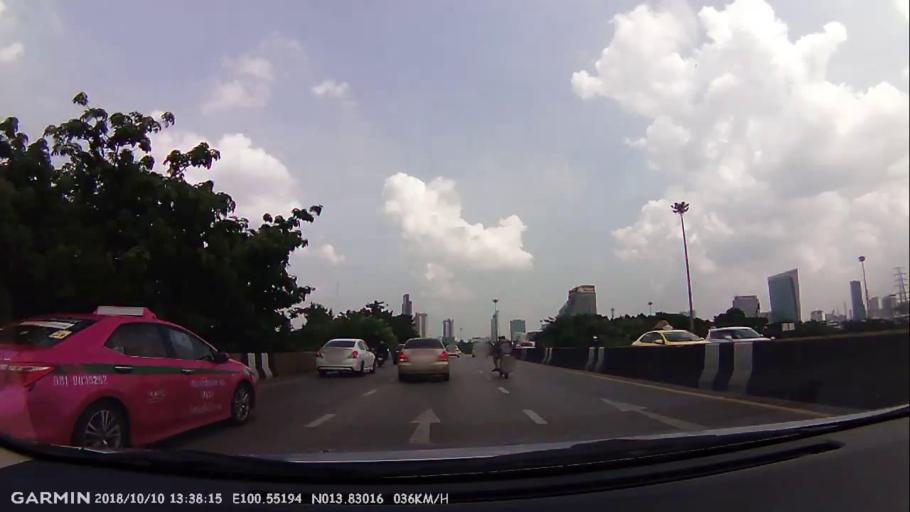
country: TH
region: Bangkok
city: Chatuchak
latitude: 13.8304
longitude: 100.5517
